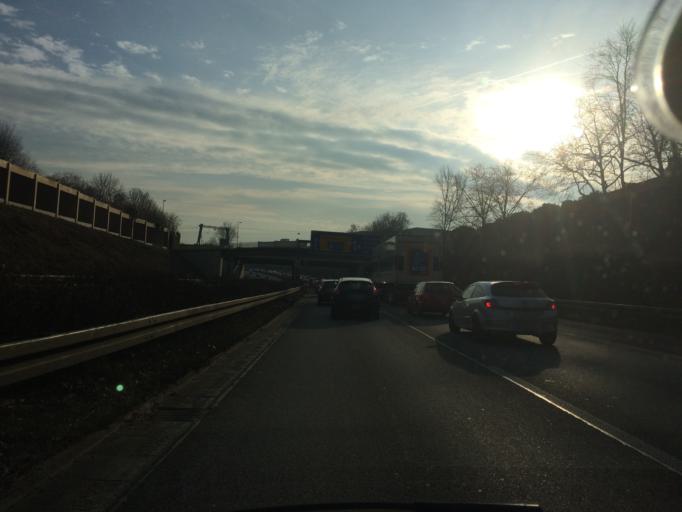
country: DE
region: North Rhine-Westphalia
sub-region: Regierungsbezirk Dusseldorf
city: Oberhausen
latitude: 51.5080
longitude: 6.8570
